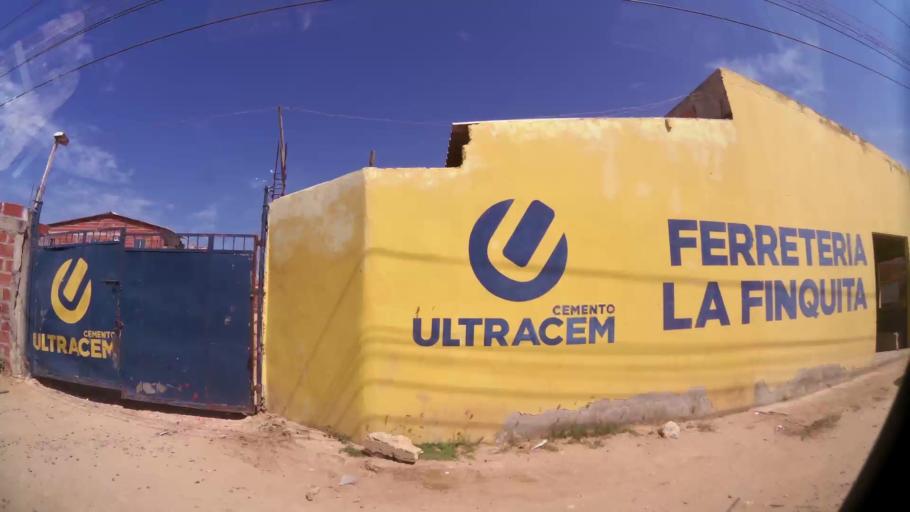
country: CO
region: Atlantico
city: Barranquilla
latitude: 10.9764
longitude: -74.8492
